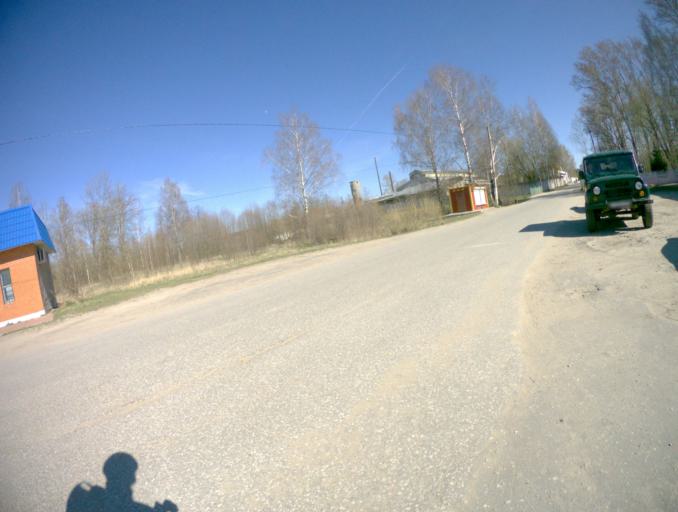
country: RU
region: Vladimir
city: Ivanishchi
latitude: 55.7746
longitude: 40.4244
